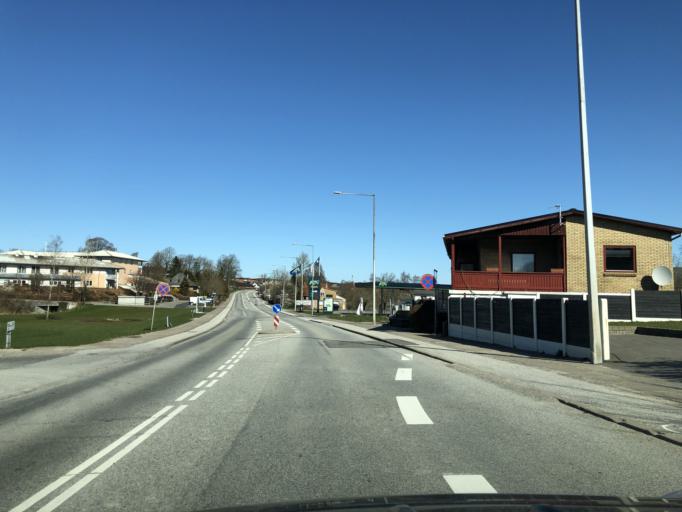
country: DK
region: North Denmark
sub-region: Rebild Kommune
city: Stovring
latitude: 56.8833
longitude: 9.8397
